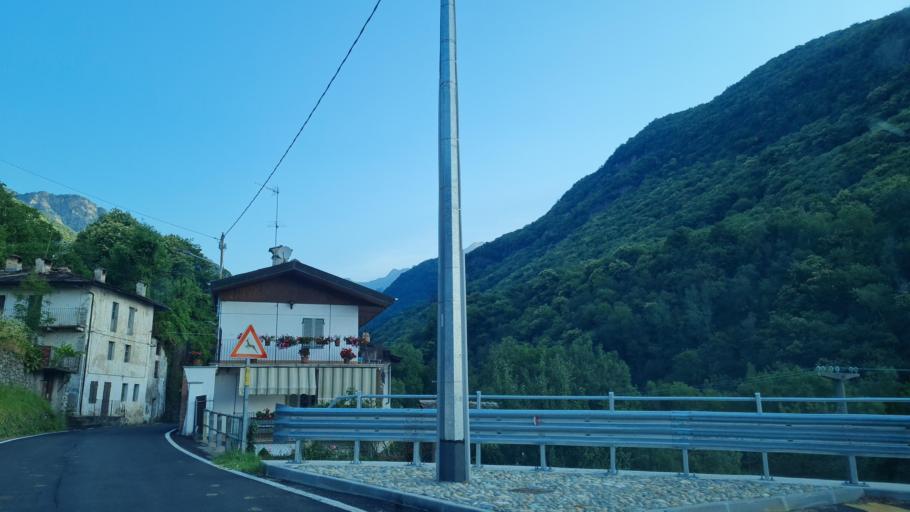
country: IT
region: Piedmont
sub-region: Provincia di Torino
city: Pont-Canavese
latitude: 45.4268
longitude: 7.5933
